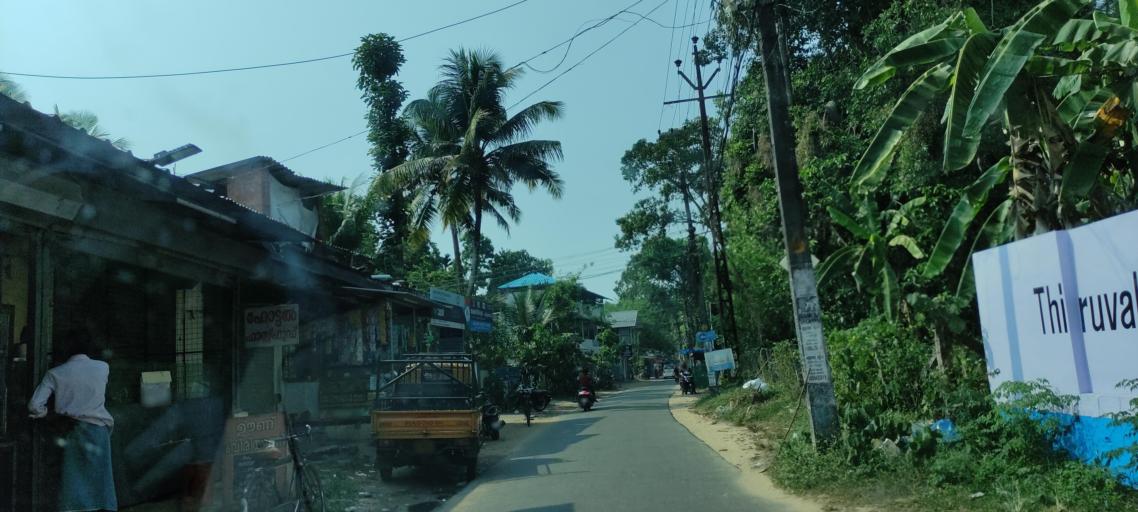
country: IN
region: Kerala
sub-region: Pattanamtitta
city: Tiruvalla
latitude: 9.3542
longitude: 76.5268
